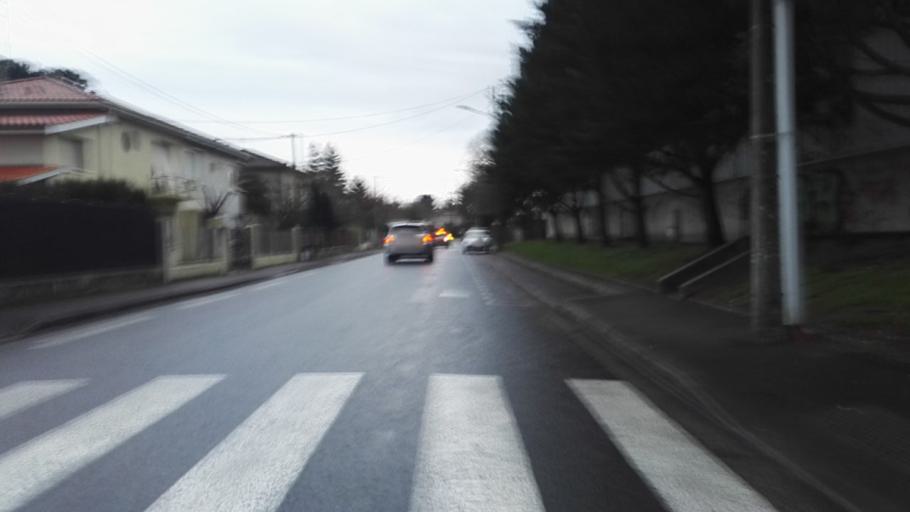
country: FR
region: Aquitaine
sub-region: Departement de la Gironde
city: Merignac
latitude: 44.8340
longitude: -0.6371
